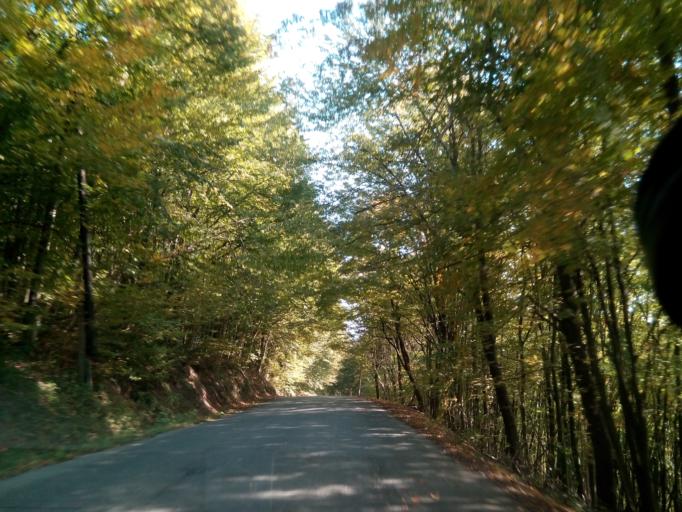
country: SK
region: Presovsky
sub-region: Okres Bardejov
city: Bardejov
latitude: 49.3608
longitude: 21.4149
